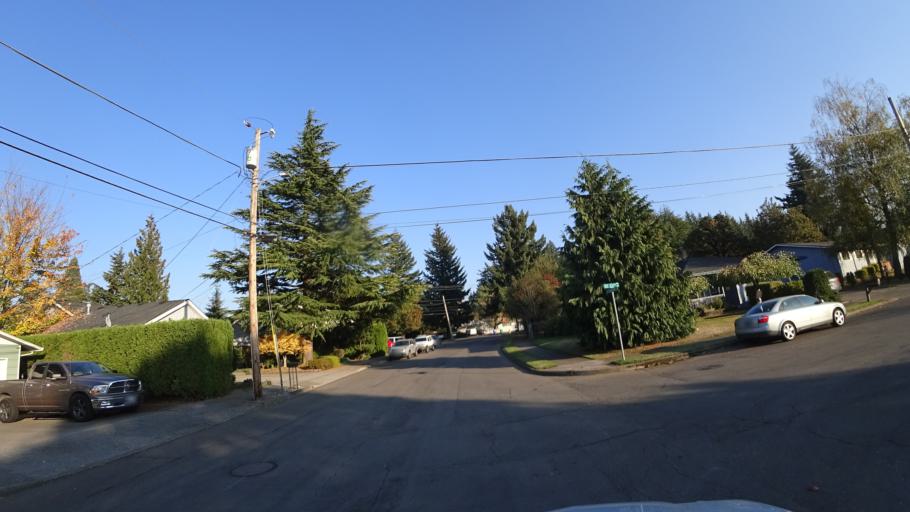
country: US
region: Oregon
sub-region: Multnomah County
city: Gresham
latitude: 45.5123
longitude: -122.4459
